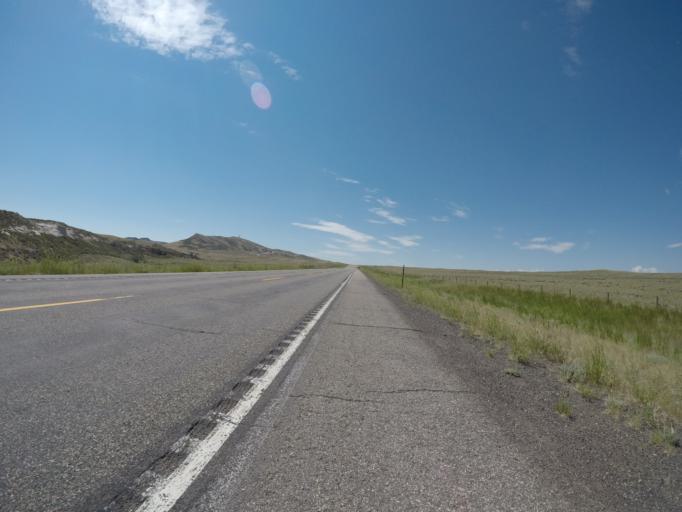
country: US
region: Wyoming
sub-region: Albany County
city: Laramie
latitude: 41.6633
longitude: -105.5339
